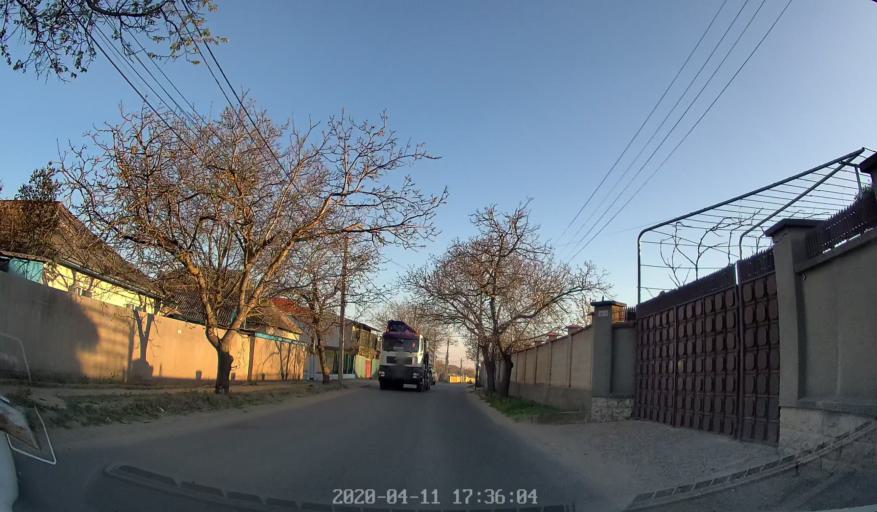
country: MD
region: Laloveni
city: Ialoveni
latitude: 46.9861
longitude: 28.8043
